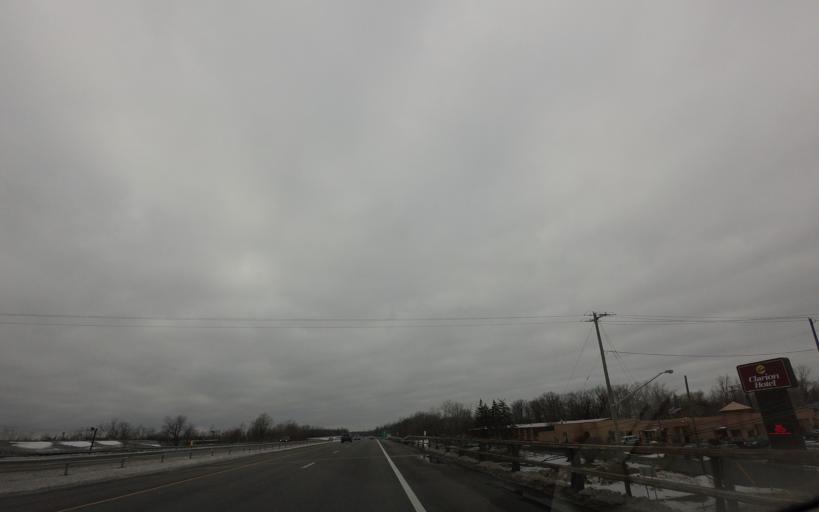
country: US
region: New York
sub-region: Erie County
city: Harris Hill
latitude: 42.9500
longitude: -78.6970
